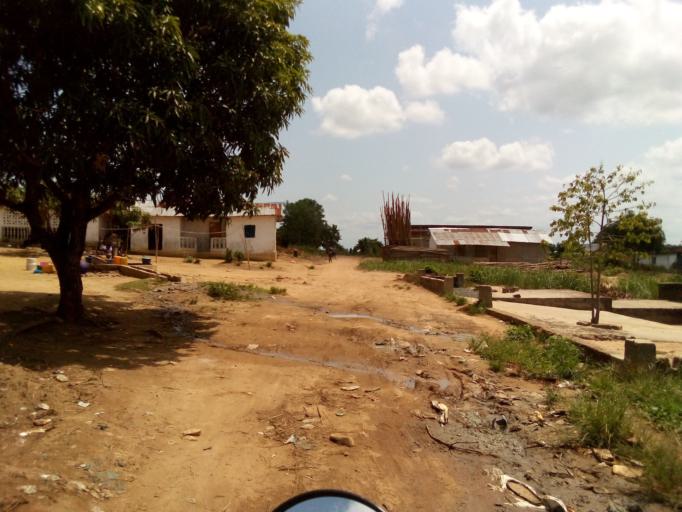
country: SL
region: Western Area
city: Waterloo
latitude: 8.3394
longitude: -13.0234
